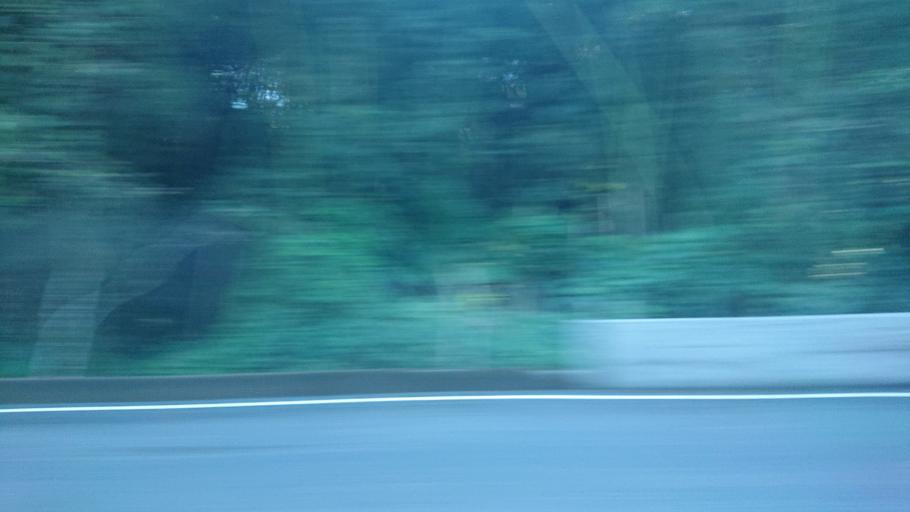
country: TW
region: Taiwan
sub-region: Chiayi
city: Jiayi Shi
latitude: 23.4602
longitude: 120.7229
